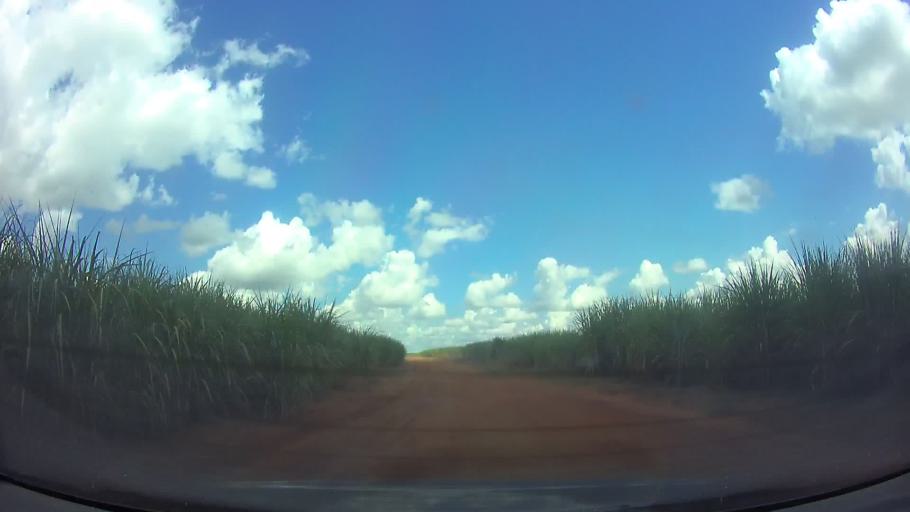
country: PY
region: Paraguari
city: La Colmena
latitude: -25.9519
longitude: -56.7672
